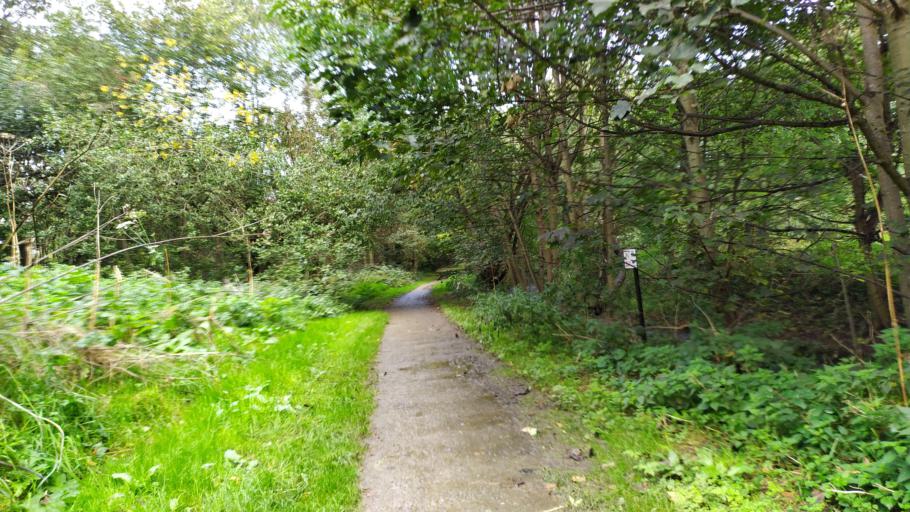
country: GB
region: England
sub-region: City and Borough of Leeds
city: Chapel Allerton
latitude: 53.8248
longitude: -1.5690
